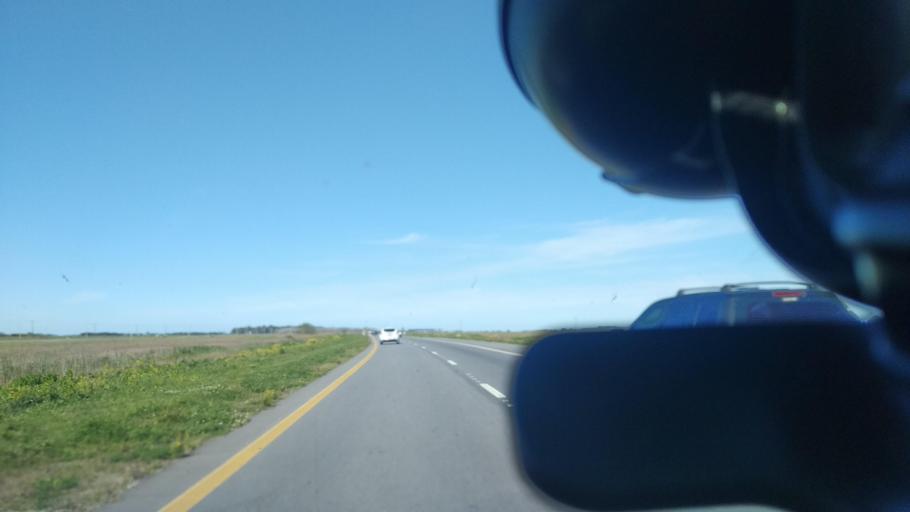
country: AR
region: Buenos Aires
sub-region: Partido de General Lavalle
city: General Lavalle
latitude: -36.4317
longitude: -56.9092
